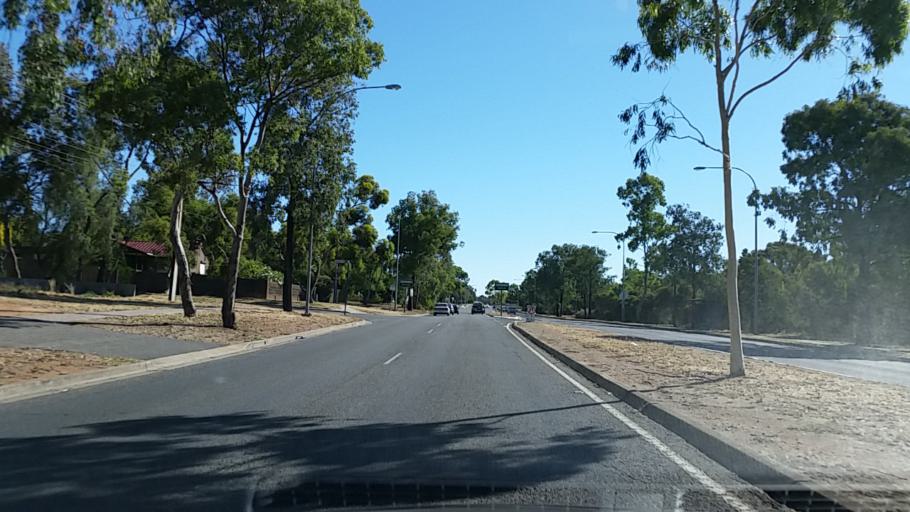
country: AU
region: South Australia
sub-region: Salisbury
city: Ingle Farm
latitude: -34.8220
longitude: 138.6378
